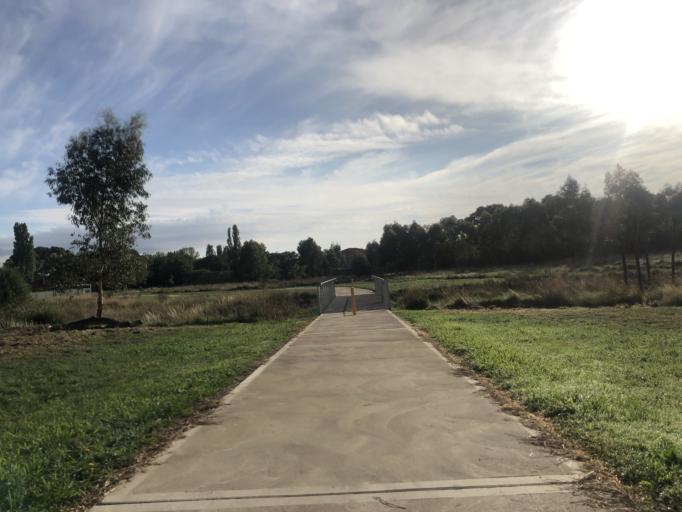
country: AU
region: New South Wales
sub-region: Orange Municipality
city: Orange
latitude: -33.2952
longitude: 149.0921
